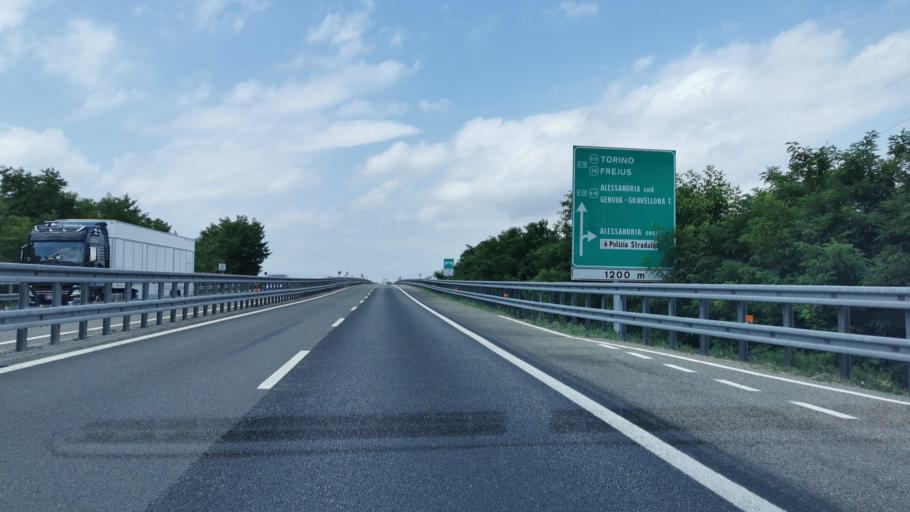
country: IT
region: Piedmont
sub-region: Provincia di Alessandria
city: Alessandria
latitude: 44.9418
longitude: 8.5992
